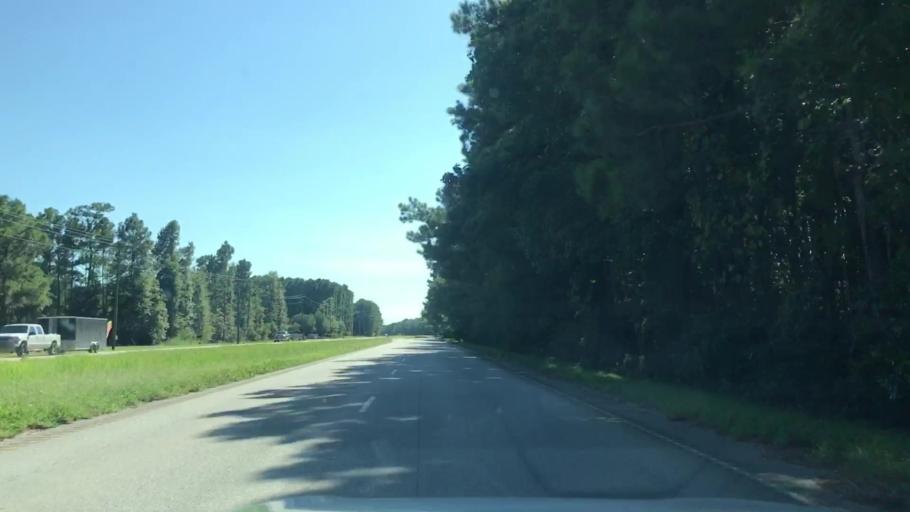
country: US
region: South Carolina
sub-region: Charleston County
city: Awendaw
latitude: 32.9841
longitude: -79.6549
